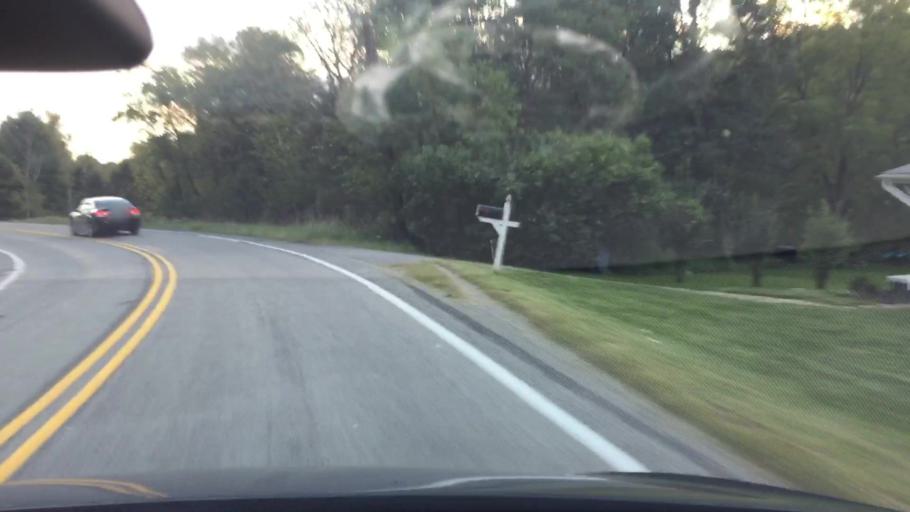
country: US
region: Pennsylvania
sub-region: Allegheny County
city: Allison Park
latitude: 40.5616
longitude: -79.9051
